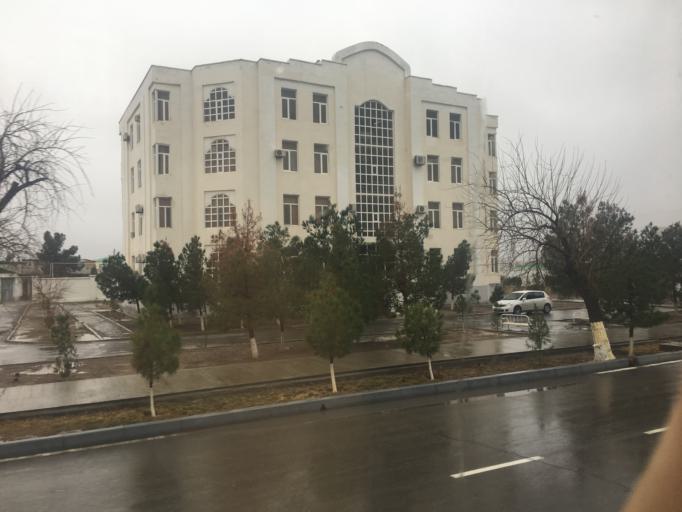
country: TM
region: Lebap
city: Turkmenabat
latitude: 39.0967
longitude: 63.5933
